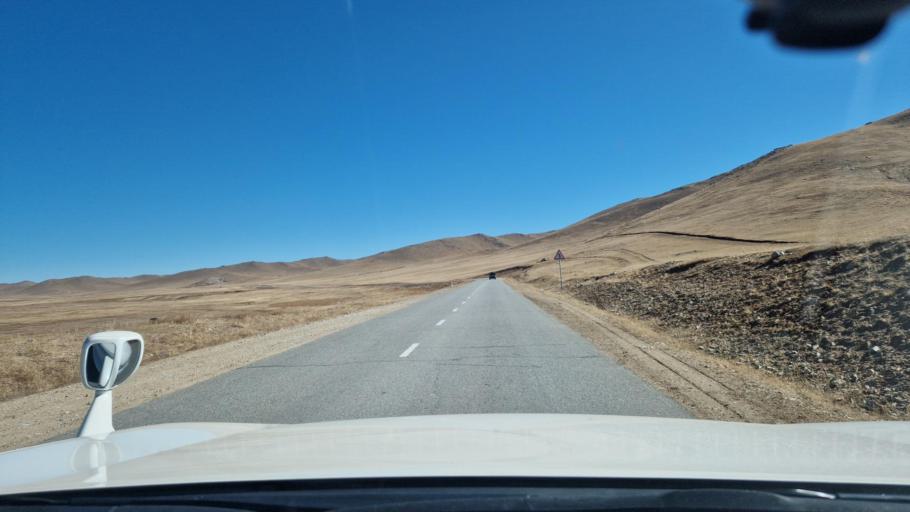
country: MN
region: Central Aimak
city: Bayandelger
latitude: 47.6933
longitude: 108.5342
